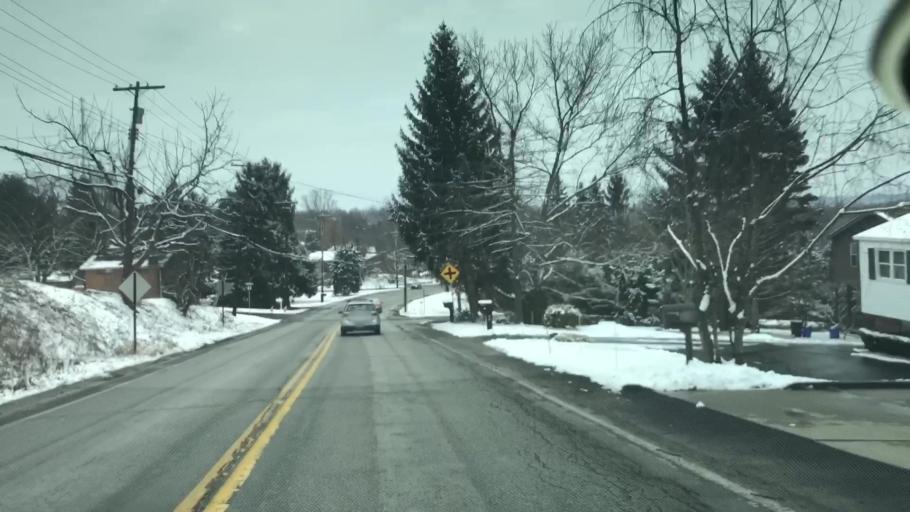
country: US
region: Pennsylvania
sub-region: Allegheny County
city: Monroeville
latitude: 40.4553
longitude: -79.7604
